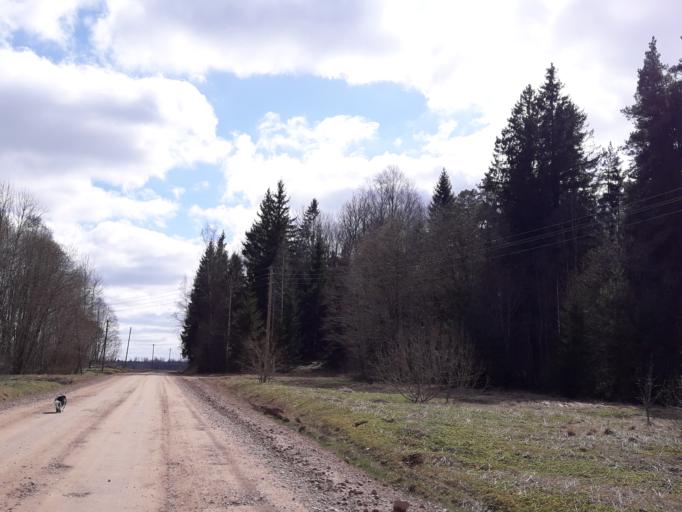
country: LV
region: Talsu Rajons
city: Sabile
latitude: 56.9074
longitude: 22.3997
